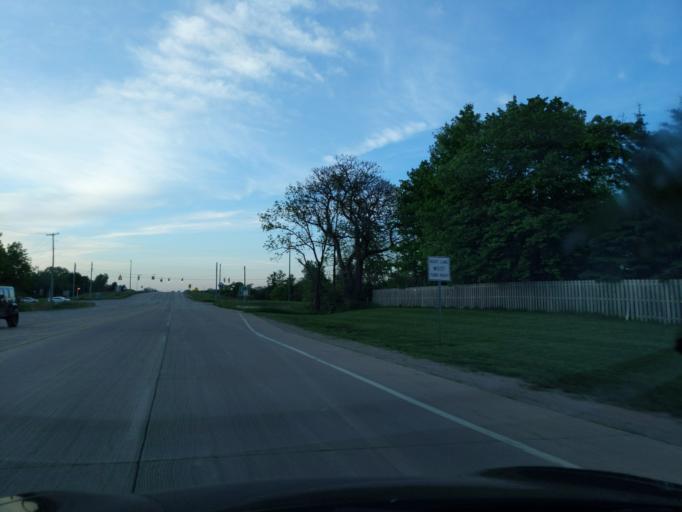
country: US
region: Michigan
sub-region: Ingham County
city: Okemos
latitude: 42.6754
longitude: -84.4328
